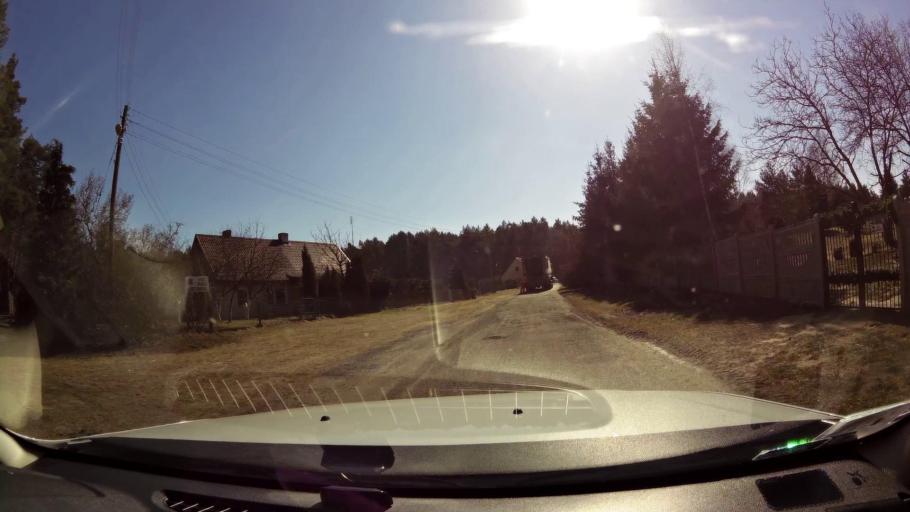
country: PL
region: West Pomeranian Voivodeship
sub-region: Powiat gryfinski
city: Banie
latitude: 53.0342
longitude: 14.6319
